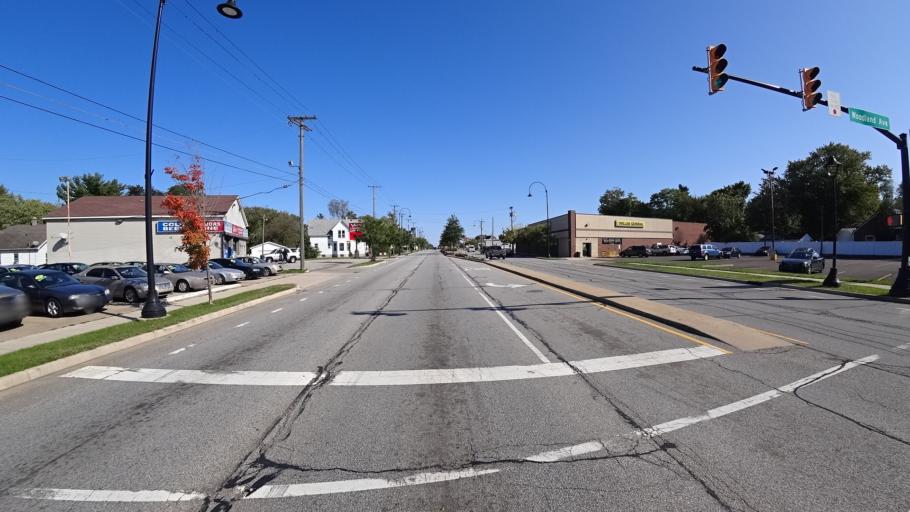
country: US
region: Indiana
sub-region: LaPorte County
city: Trail Creek
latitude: 41.7100
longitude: -86.8746
